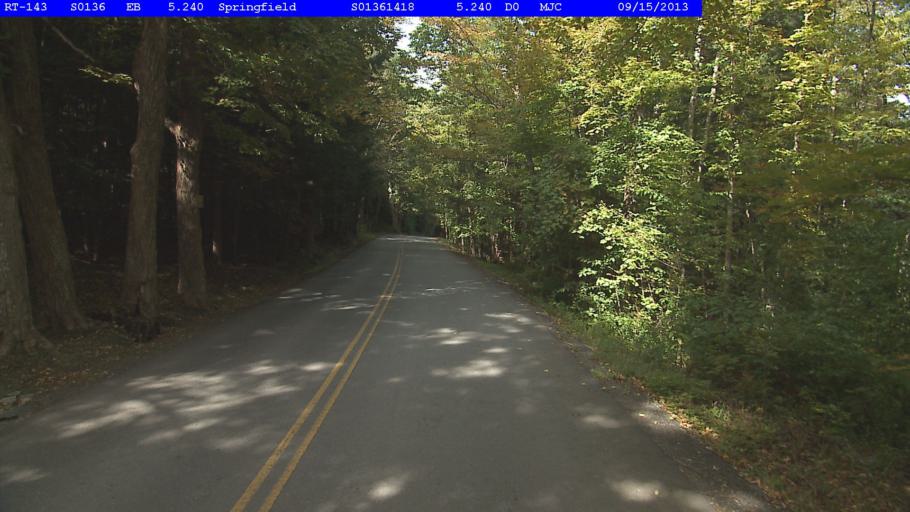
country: US
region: Vermont
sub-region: Windsor County
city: Springfield
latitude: 43.3241
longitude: -72.4121
